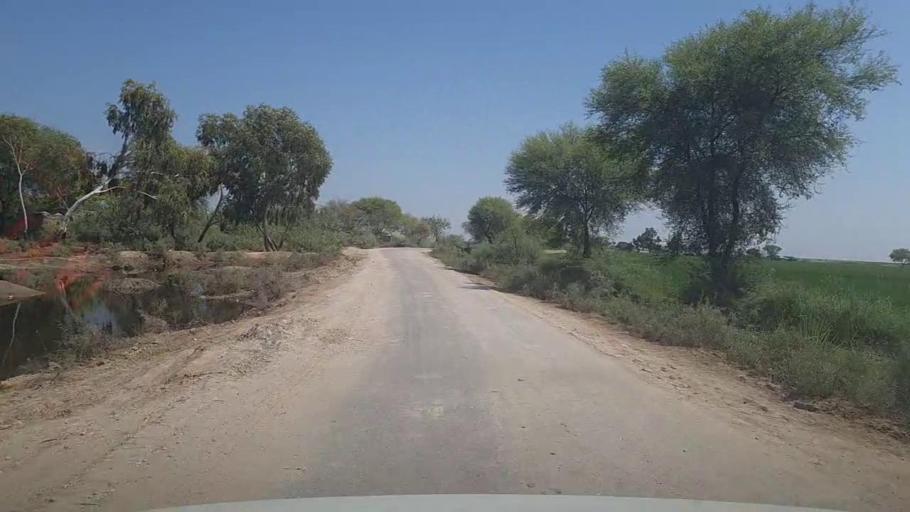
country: PK
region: Sindh
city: Kashmor
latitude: 28.2844
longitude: 69.4373
